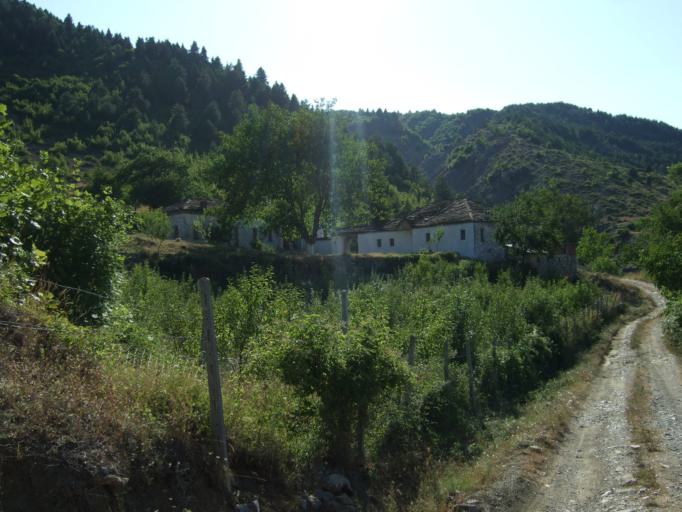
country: AL
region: Gjirokaster
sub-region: Rrethi i Permetit
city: Frasher
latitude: 40.3606
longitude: 20.4288
